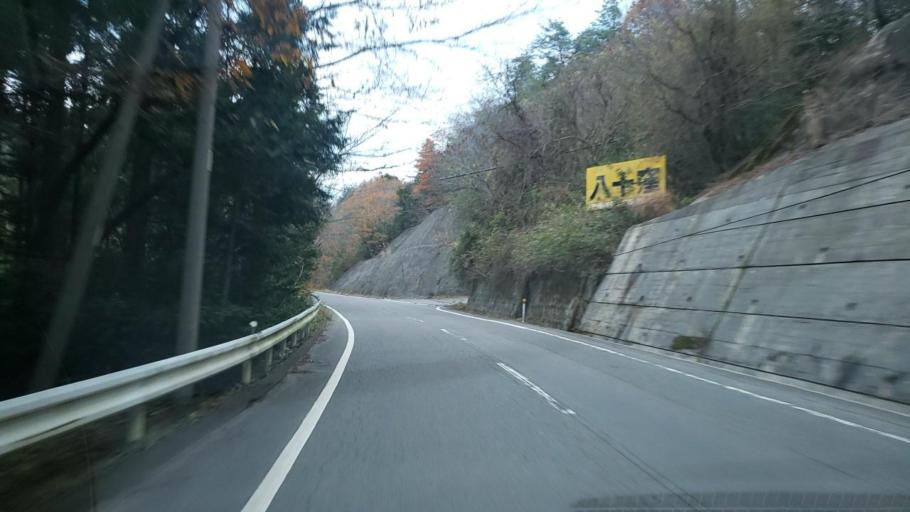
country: JP
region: Tokushima
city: Wakimachi
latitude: 34.1832
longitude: 134.1978
